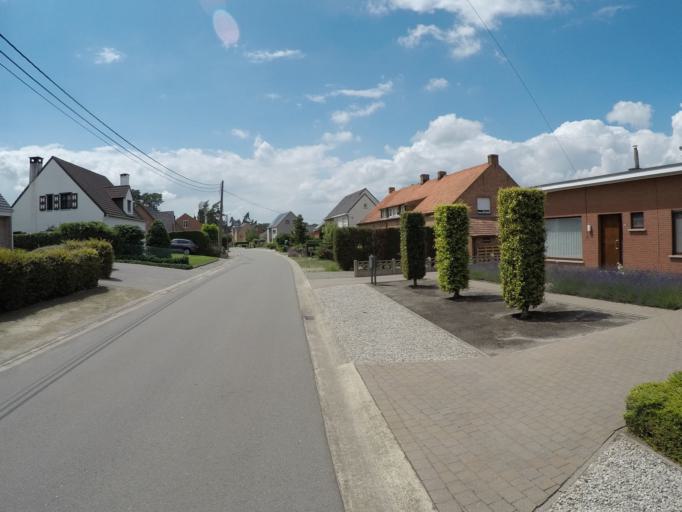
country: BE
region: Flanders
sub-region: Provincie Antwerpen
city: Lille
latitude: 51.2673
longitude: 4.7934
